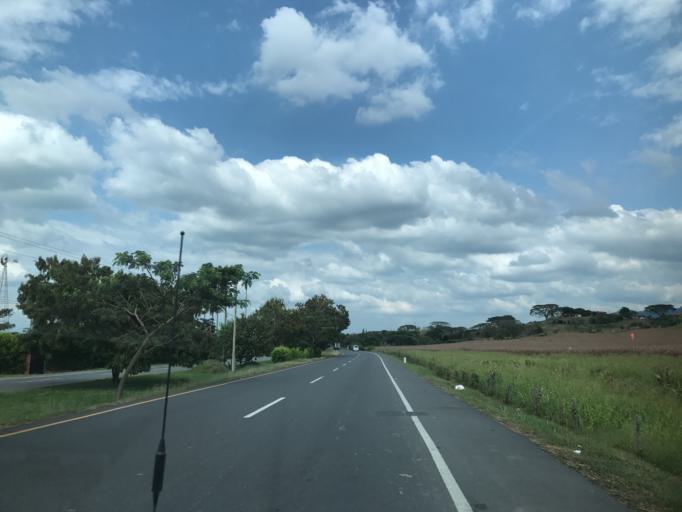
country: CO
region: Valle del Cauca
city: Obando
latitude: 4.5898
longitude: -75.9680
